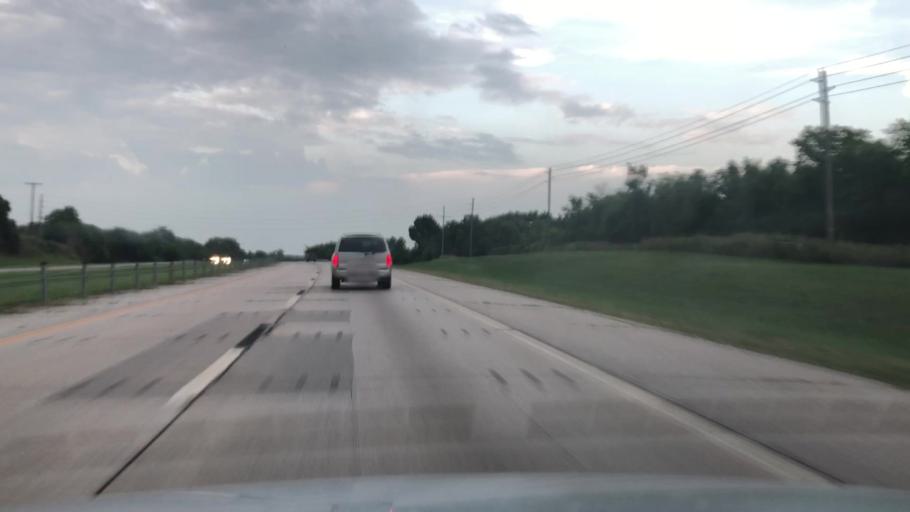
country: US
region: Oklahoma
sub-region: Tulsa County
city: Turley
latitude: 36.2179
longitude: -95.9442
